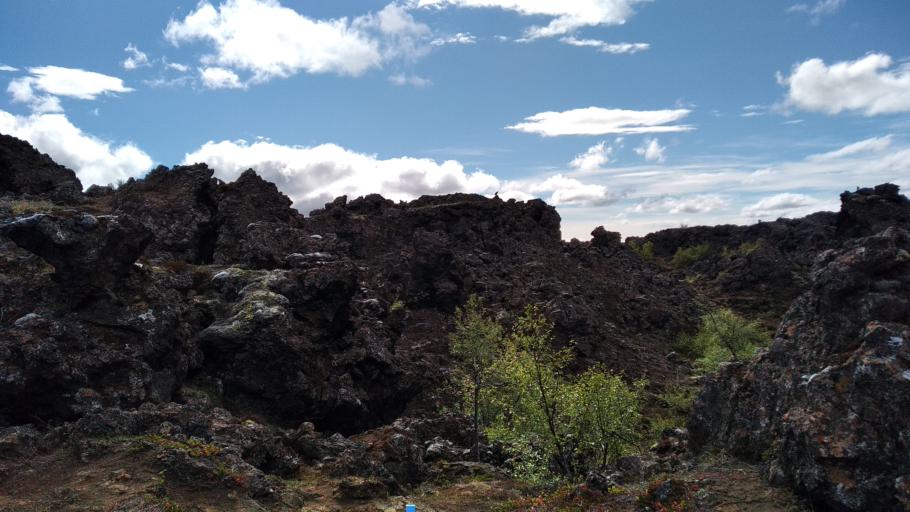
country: IS
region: Northeast
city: Laugar
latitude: 65.5884
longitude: -16.9100
